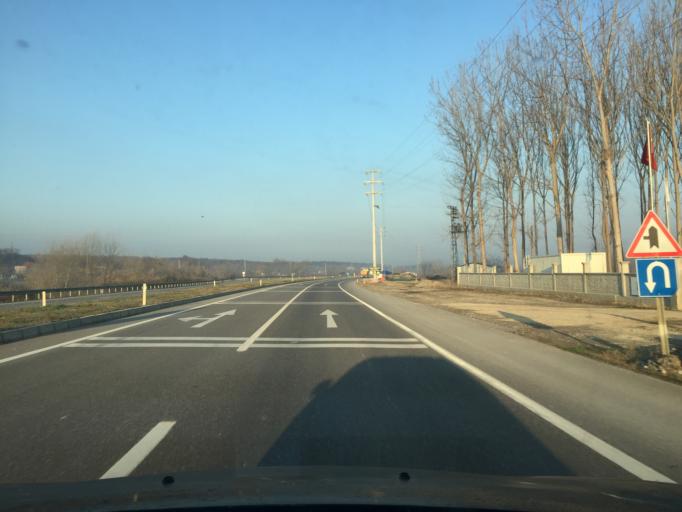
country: TR
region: Sakarya
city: Akyazi
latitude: 40.6478
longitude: 30.6079
